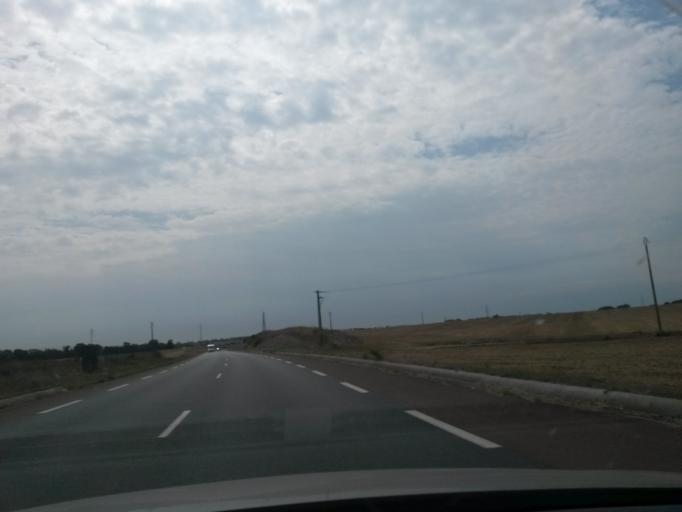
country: FR
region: Poitou-Charentes
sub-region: Departement de la Charente-Maritime
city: Saint-Xandre
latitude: 46.2118
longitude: -1.0907
